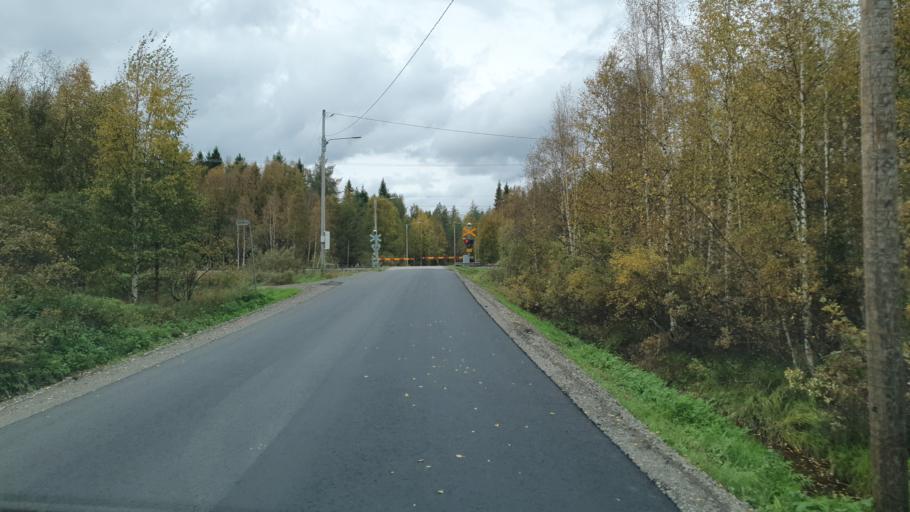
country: FI
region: Lapland
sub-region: Rovaniemi
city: Rovaniemi
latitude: 66.4203
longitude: 25.4091
